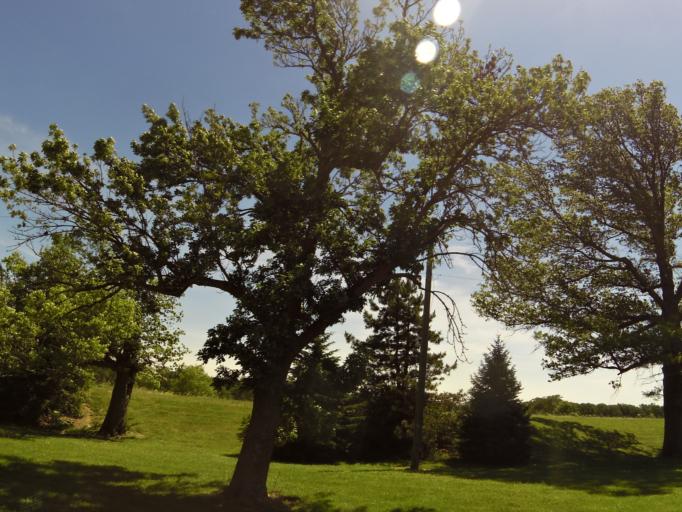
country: US
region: Illinois
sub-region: Vermilion County
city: Rossville
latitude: 40.2569
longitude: -87.6485
